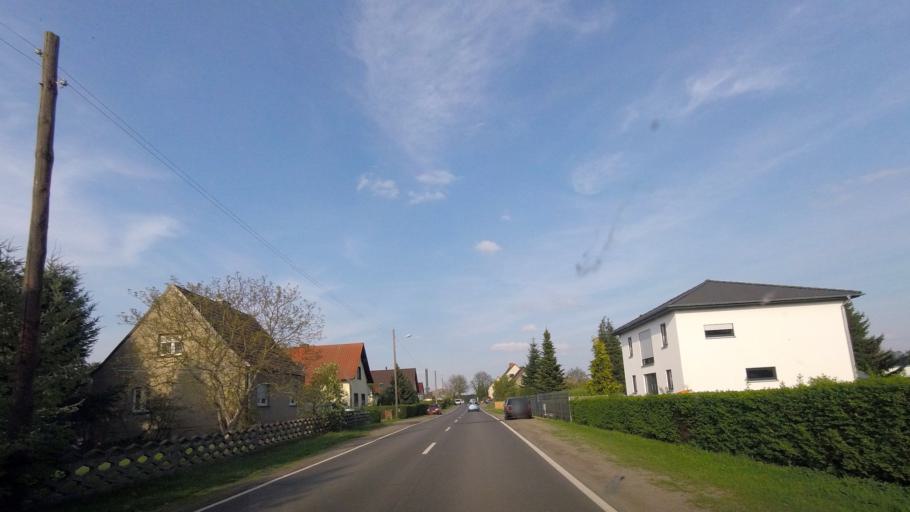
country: DE
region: Saxony-Anhalt
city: Abtsdorf
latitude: 51.8750
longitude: 12.7002
